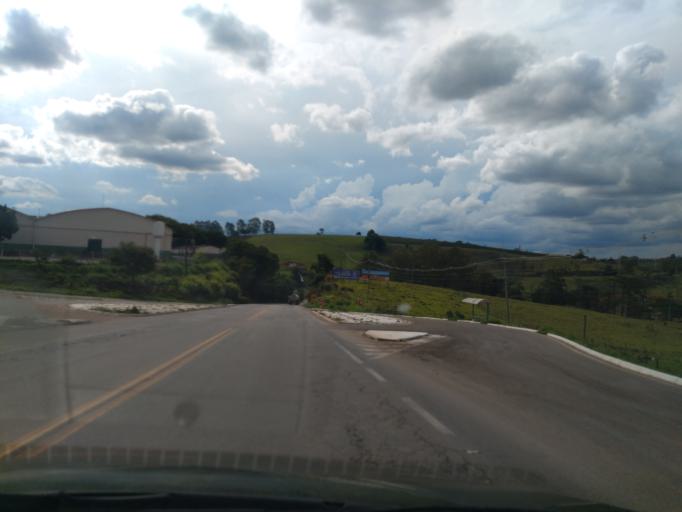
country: BR
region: Minas Gerais
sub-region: Varginha
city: Varginha
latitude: -21.6134
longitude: -45.4263
